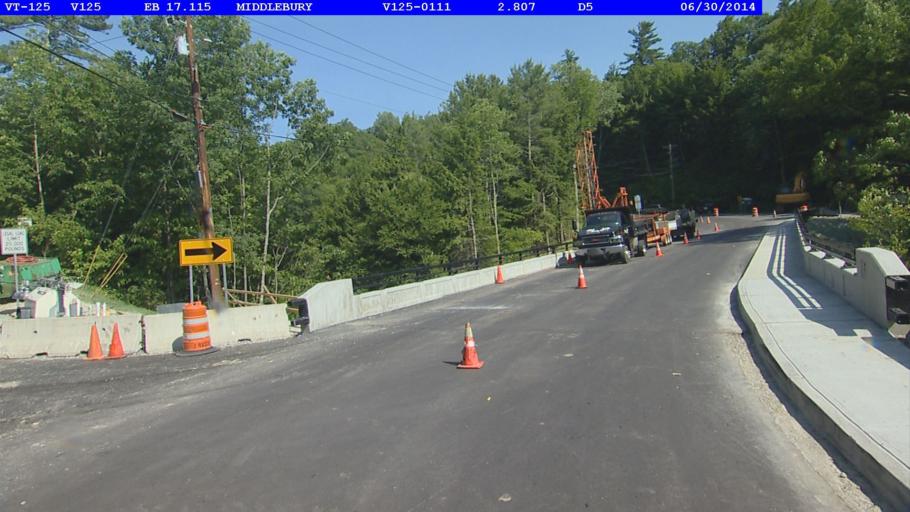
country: US
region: Vermont
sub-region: Addison County
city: Middlebury (village)
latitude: 43.9704
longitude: -73.0859
